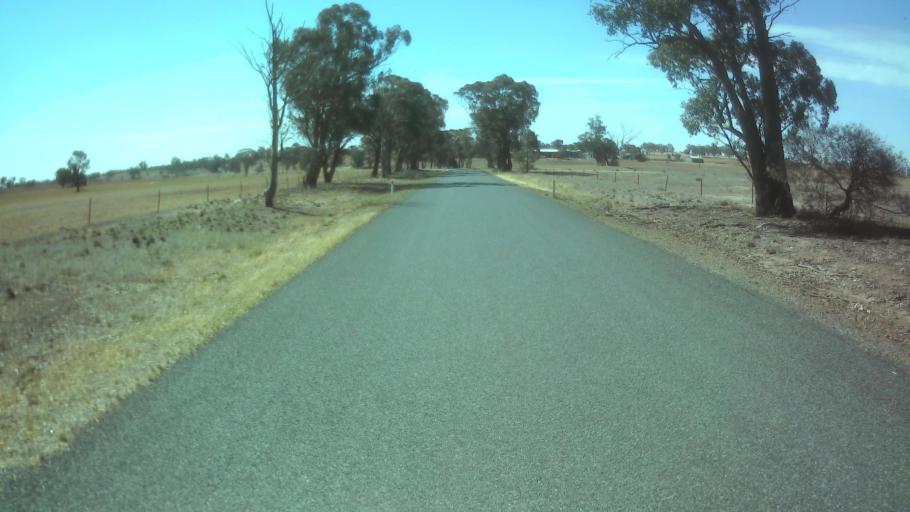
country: AU
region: New South Wales
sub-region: Weddin
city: Grenfell
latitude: -33.7660
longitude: 147.8648
